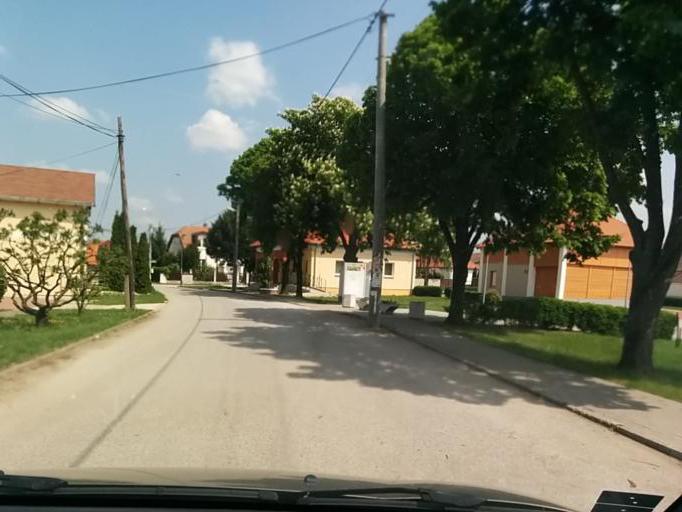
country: SK
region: Trnavsky
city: Sladkovicovo
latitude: 48.2230
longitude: 17.6422
